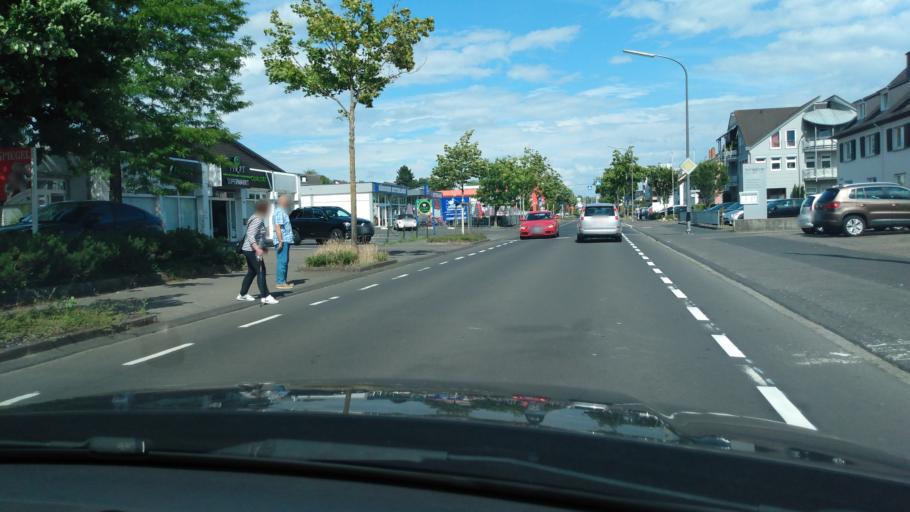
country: DE
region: Rheinland-Pfalz
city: Wittlich
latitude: 49.9880
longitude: 6.8975
